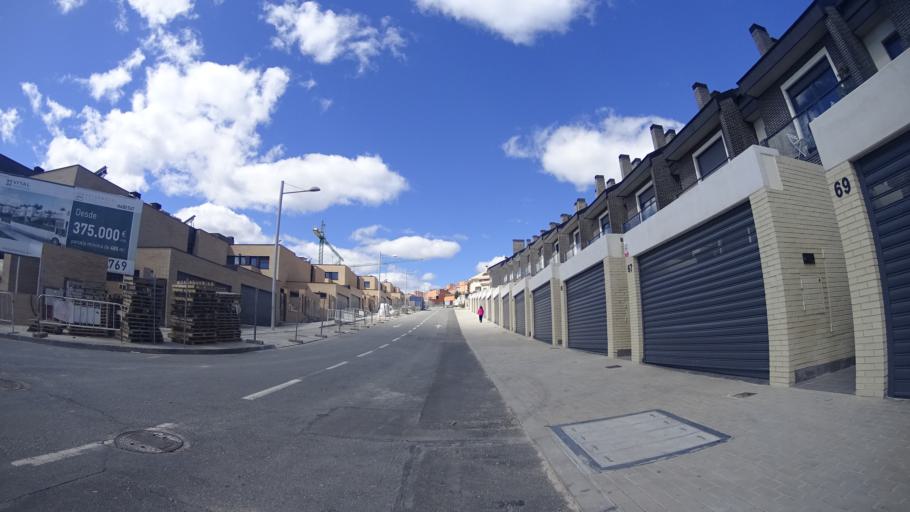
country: ES
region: Madrid
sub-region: Provincia de Madrid
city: Torrelodones
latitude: 40.5633
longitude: -3.9184
